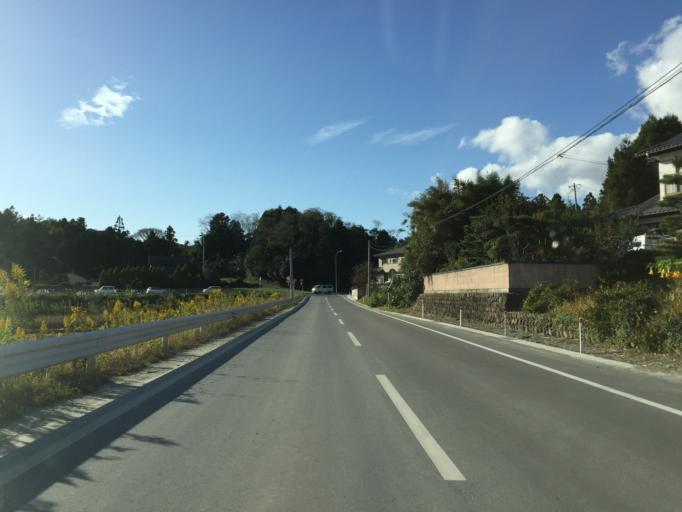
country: JP
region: Miyagi
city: Marumori
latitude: 37.8839
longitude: 140.9155
